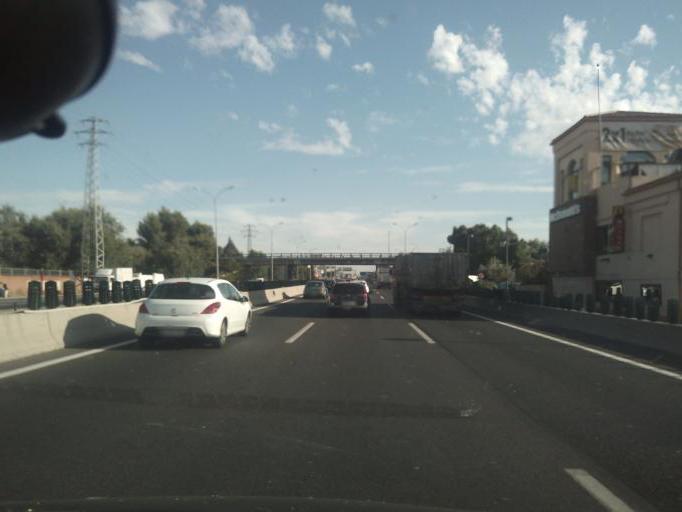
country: ES
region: Madrid
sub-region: Provincia de Madrid
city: Pinto
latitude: 40.2465
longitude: -3.6899
